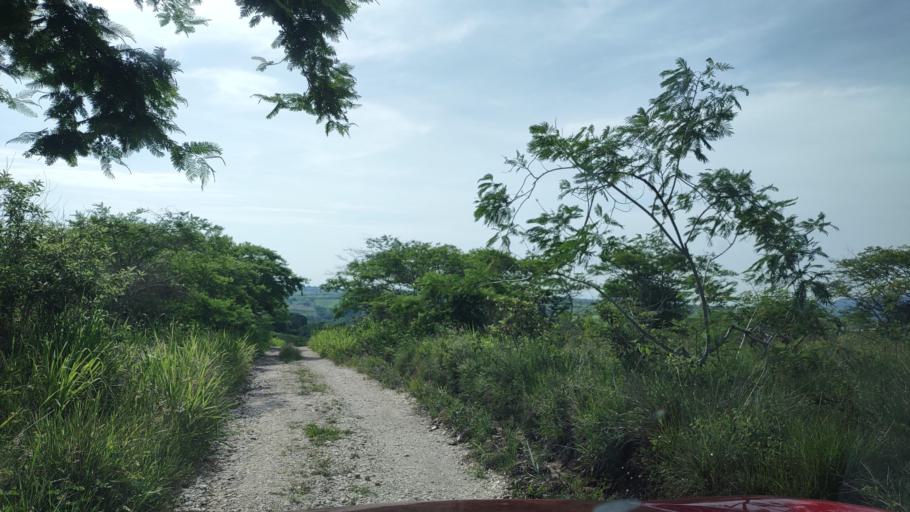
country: MX
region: Veracruz
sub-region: Emiliano Zapata
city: Dos Rios
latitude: 19.4734
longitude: -96.8222
